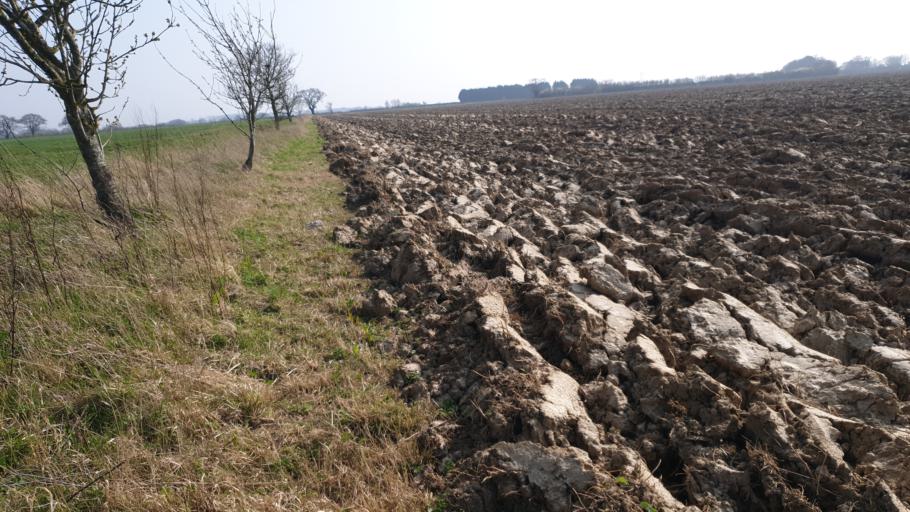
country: GB
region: England
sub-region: Essex
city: Mistley
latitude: 51.9057
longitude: 1.1277
